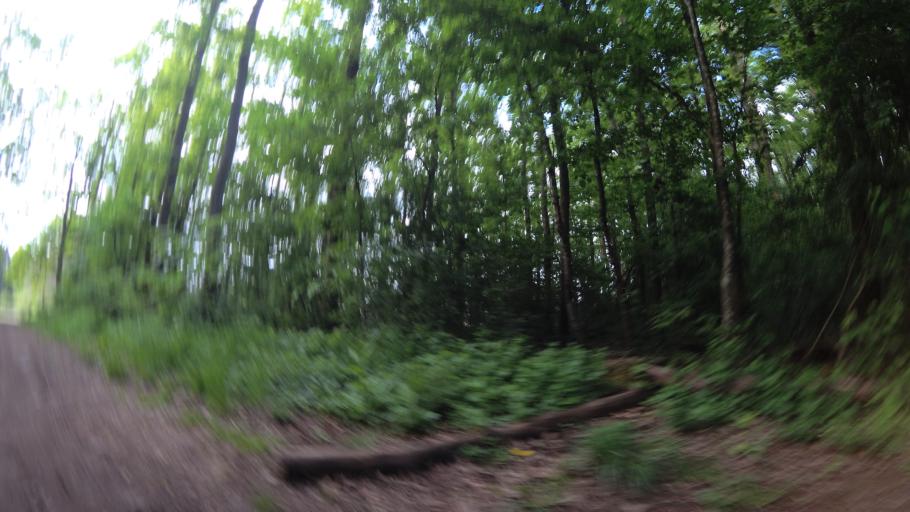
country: DE
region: Saarland
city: Neunkirchen
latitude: 49.3605
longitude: 7.1878
